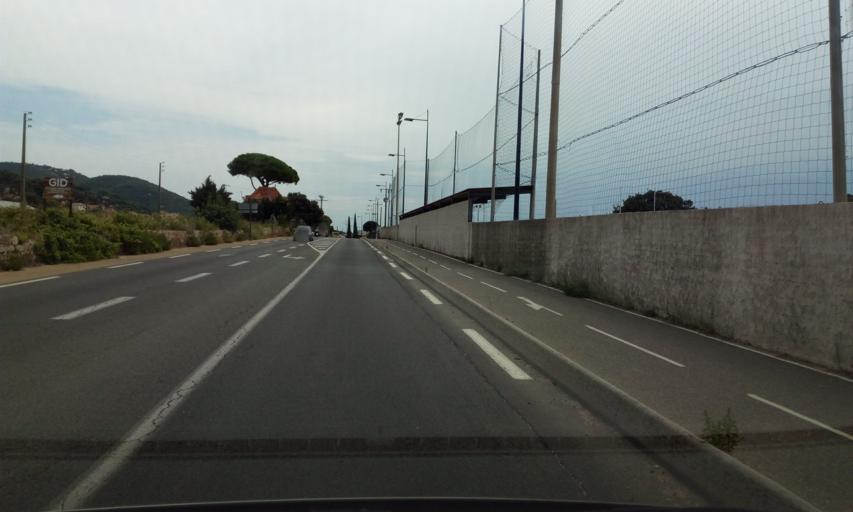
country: FR
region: Provence-Alpes-Cote d'Azur
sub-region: Departement du Var
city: Carqueiranne
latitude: 43.1008
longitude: 6.0601
